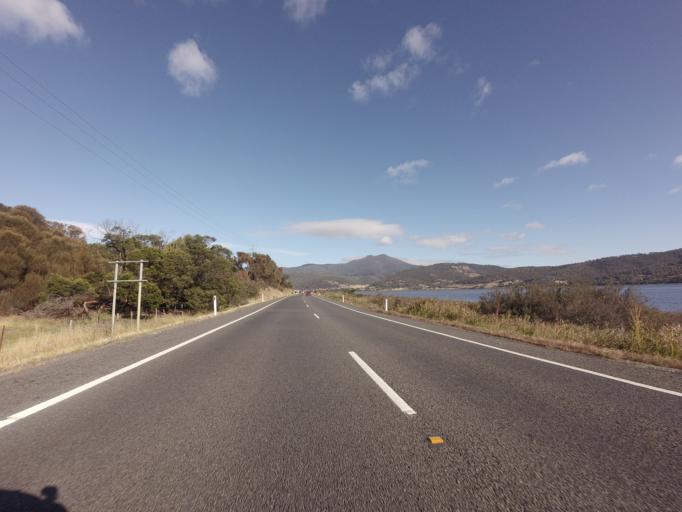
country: AU
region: Tasmania
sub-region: Brighton
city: Bridgewater
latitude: -42.7409
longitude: 147.2051
